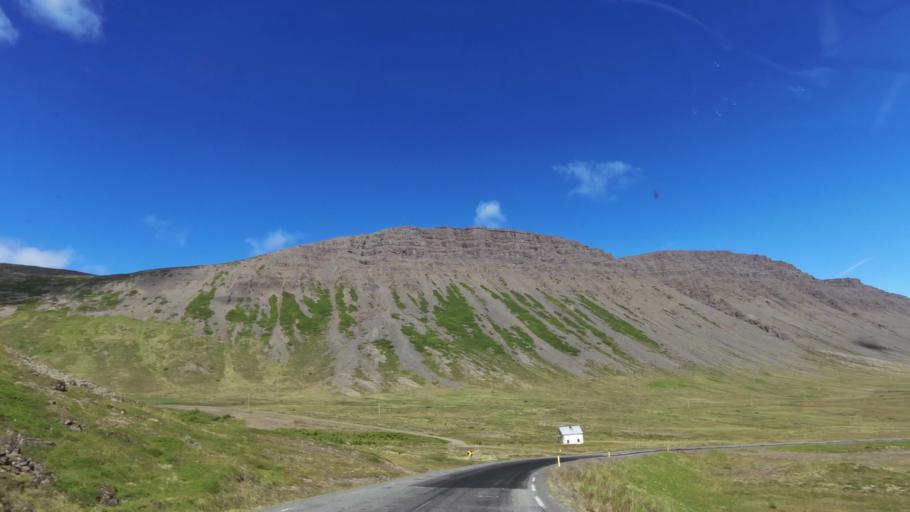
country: IS
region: Westfjords
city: Isafjoerdur
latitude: 65.6640
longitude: -23.6402
